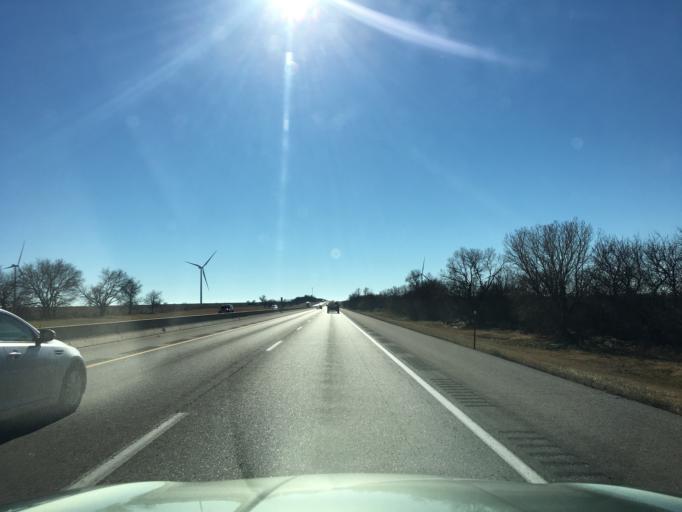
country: US
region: Kansas
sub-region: Sumner County
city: Wellington
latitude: 37.1389
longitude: -97.3393
